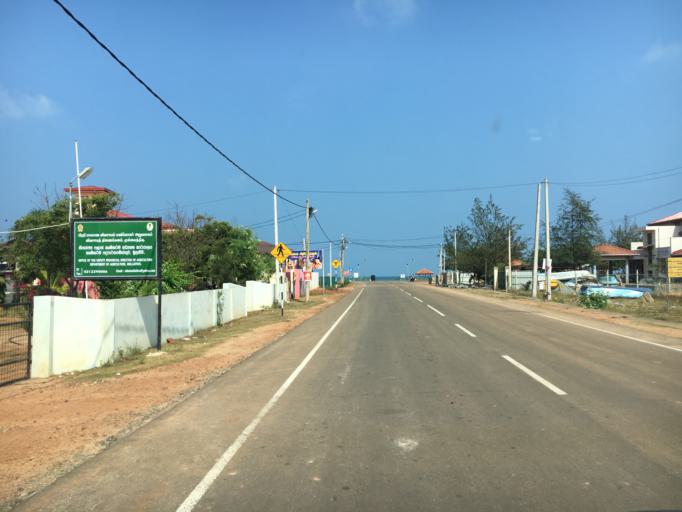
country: LK
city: Padaviya Divisional Secretariat
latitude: 9.2713
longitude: 80.8178
